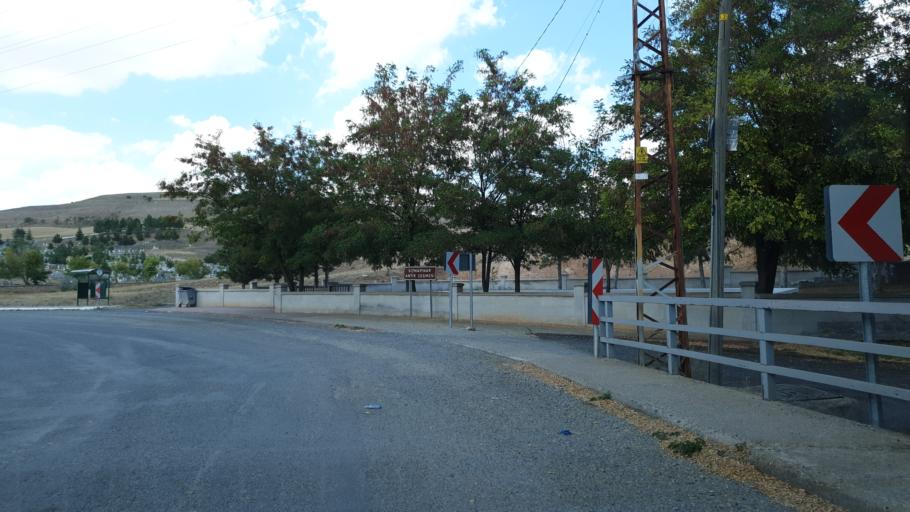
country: TR
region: Kayseri
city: Felahiye
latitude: 39.0940
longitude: 35.5633
